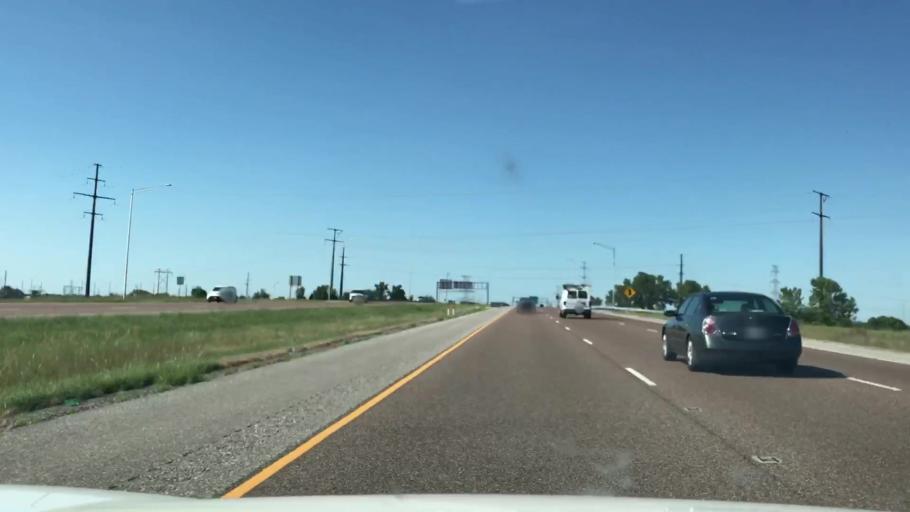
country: US
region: Illinois
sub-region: Madison County
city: Pontoon Beach
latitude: 38.7307
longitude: -90.0375
